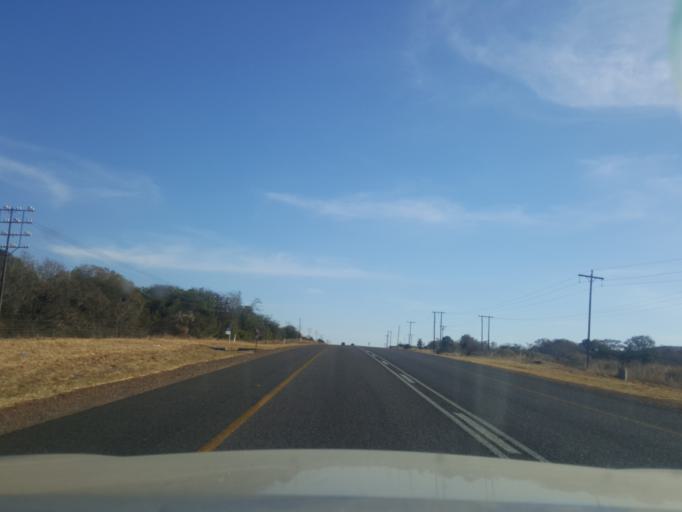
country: ZA
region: North-West
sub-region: Ngaka Modiri Molema District Municipality
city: Zeerust
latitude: -25.5249
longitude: 26.1538
